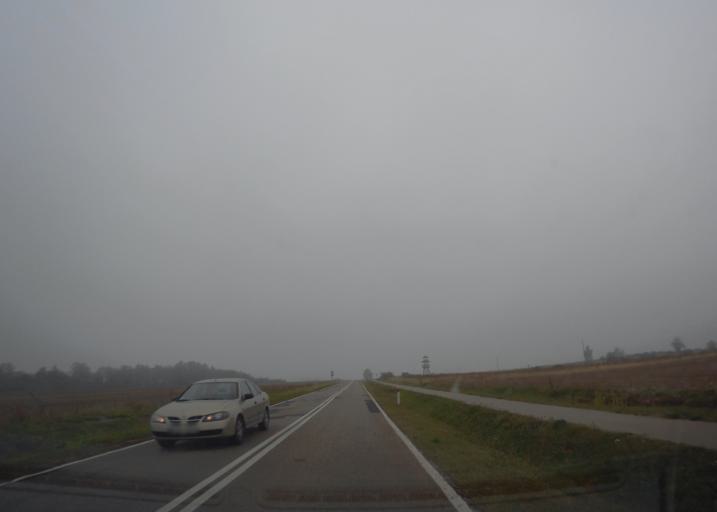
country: PL
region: Lublin Voivodeship
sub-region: Powiat bialski
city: Slawatycze
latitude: 51.6580
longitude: 23.5205
